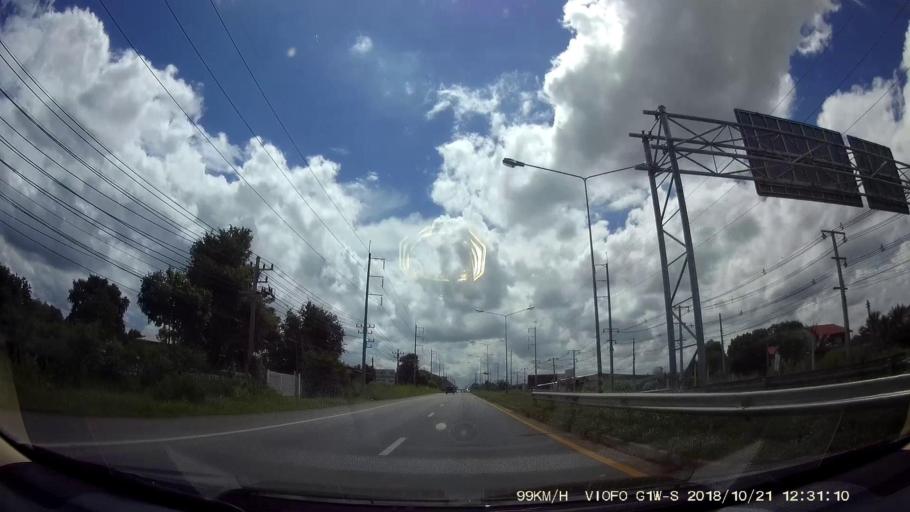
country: TH
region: Nakhon Ratchasima
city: Dan Khun Thot
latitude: 15.1605
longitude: 101.7361
